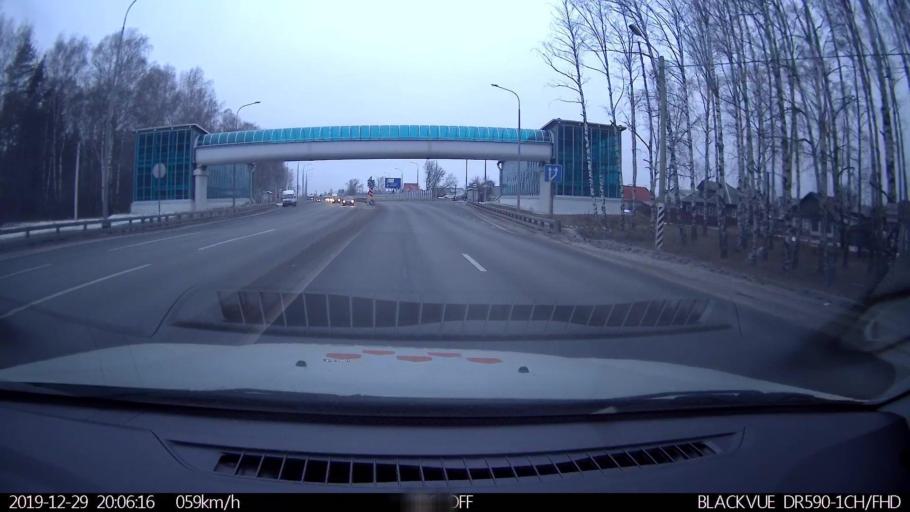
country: RU
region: Nizjnij Novgorod
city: Neklyudovo
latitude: 56.3951
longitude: 44.0068
